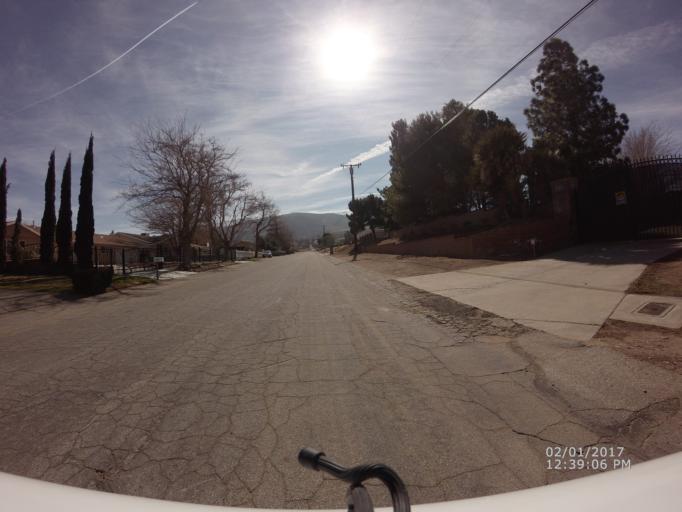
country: US
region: California
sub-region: Los Angeles County
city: Desert View Highlands
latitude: 34.5568
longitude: -118.1500
